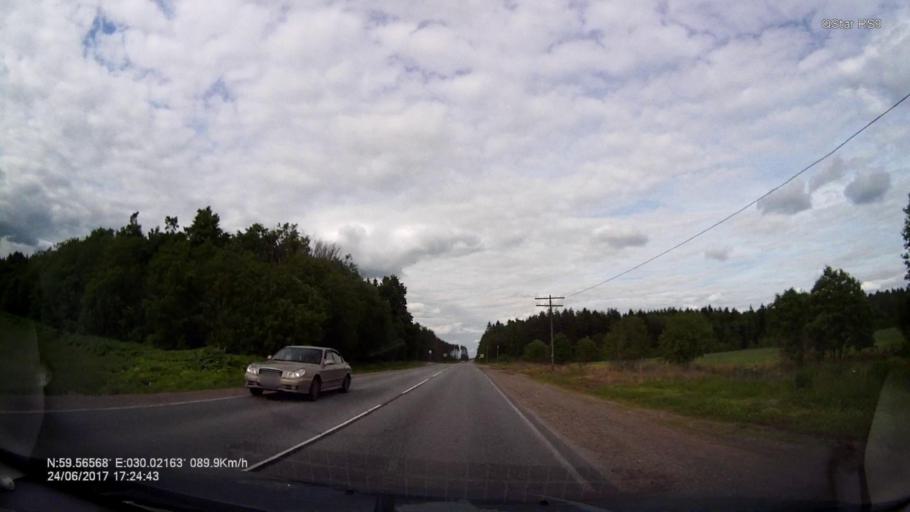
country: RU
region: Leningrad
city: Mariyenburg
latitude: 59.5658
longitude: 30.0219
